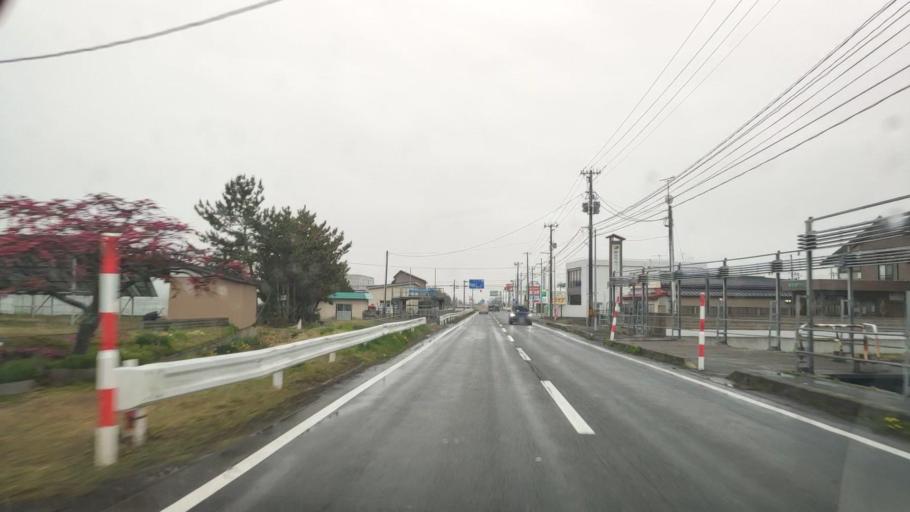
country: JP
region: Akita
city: Noshiromachi
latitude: 40.1039
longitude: 140.0040
